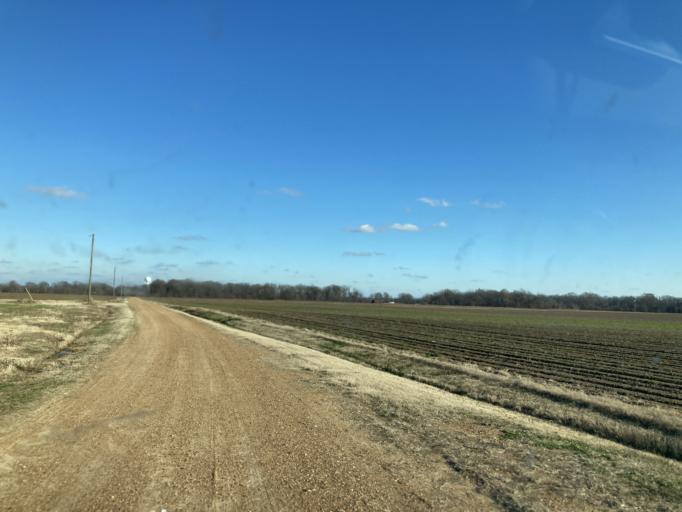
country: US
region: Mississippi
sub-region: Yazoo County
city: Yazoo City
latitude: 32.9233
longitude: -90.5071
